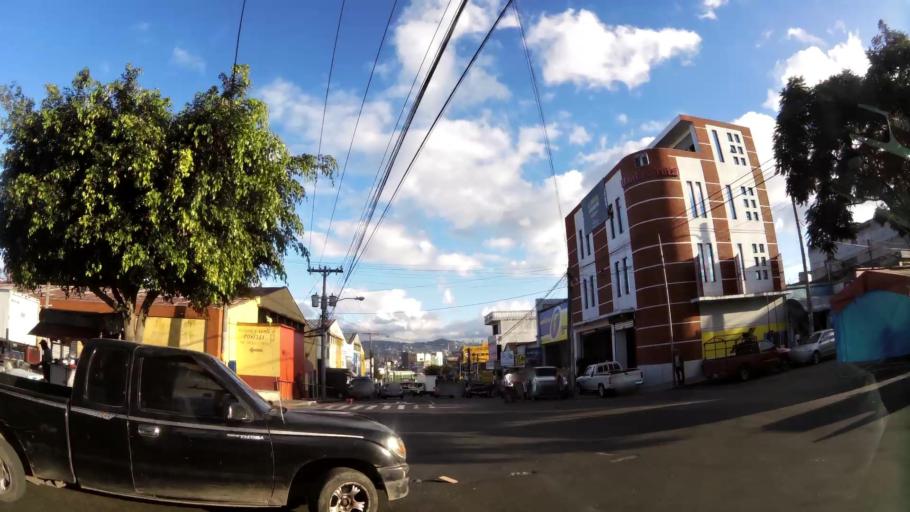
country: GT
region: Guatemala
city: Guatemala City
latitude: 14.6211
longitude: -90.5226
